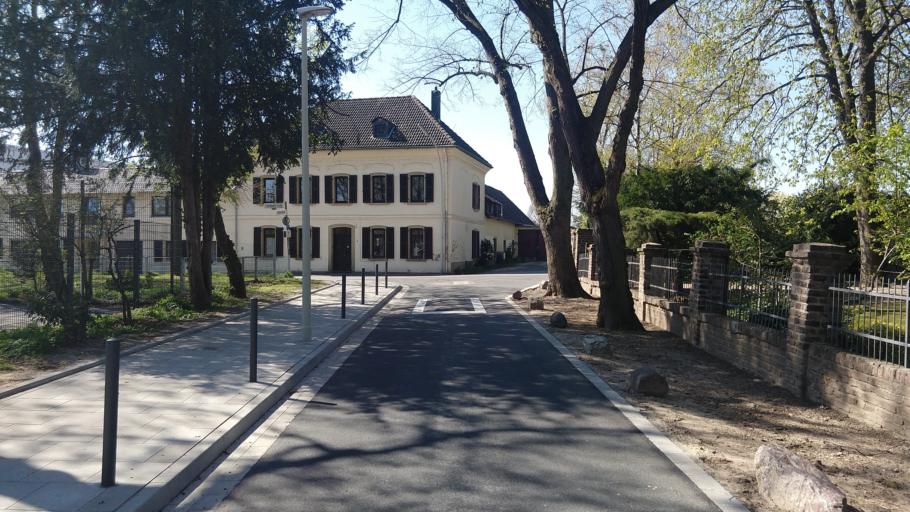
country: DE
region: North Rhine-Westphalia
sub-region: Regierungsbezirk Koln
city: Alfter
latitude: 50.7611
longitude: 7.0486
